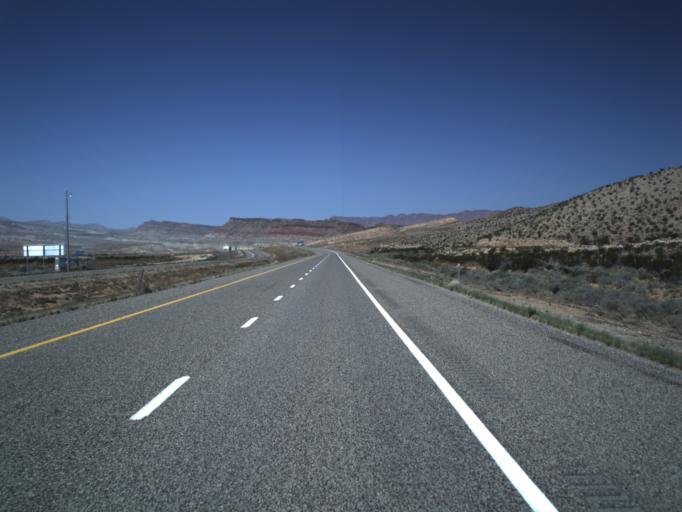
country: US
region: Utah
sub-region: Washington County
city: Saint George
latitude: 37.0117
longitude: -113.5911
